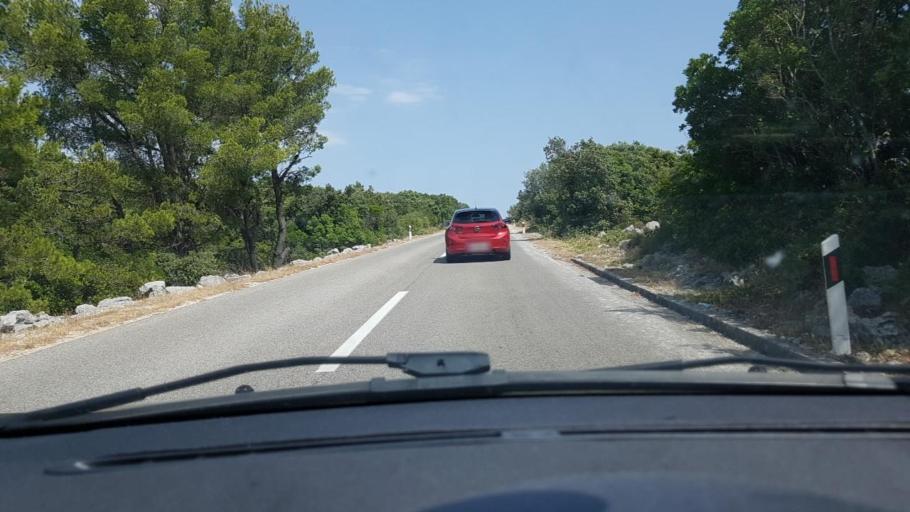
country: HR
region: Dubrovacko-Neretvanska
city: Smokvica
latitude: 42.9490
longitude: 16.9758
